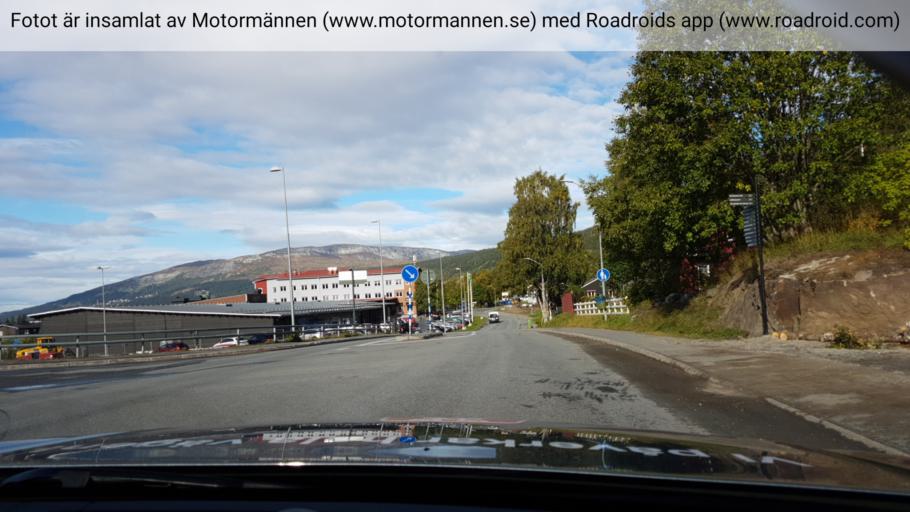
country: SE
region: Jaemtland
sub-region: Are Kommun
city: Are
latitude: 63.3953
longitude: 13.0904
